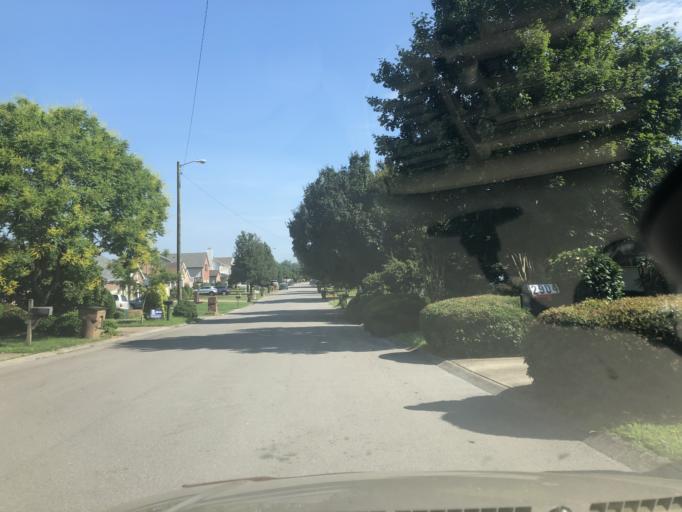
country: US
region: Tennessee
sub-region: Davidson County
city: Lakewood
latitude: 36.2368
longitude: -86.6976
